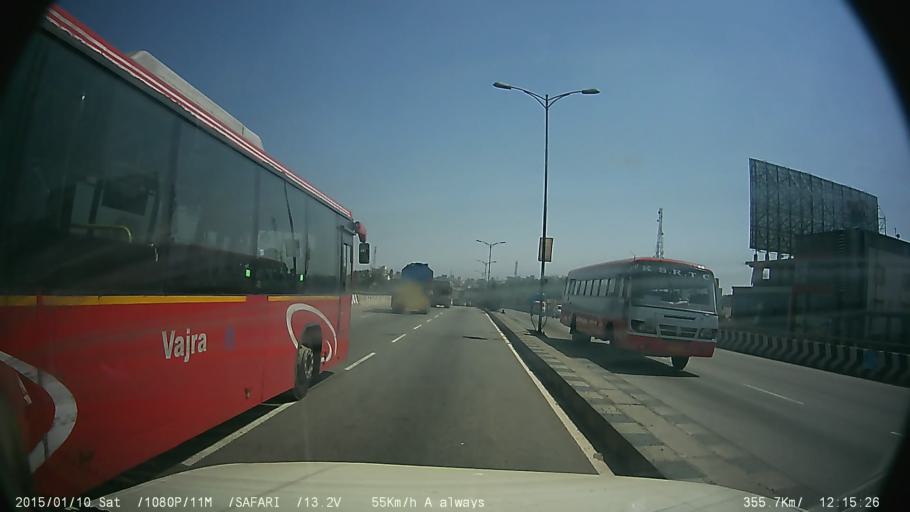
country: IN
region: Karnataka
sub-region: Bangalore Urban
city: Anekal
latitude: 12.8024
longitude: 77.7049
